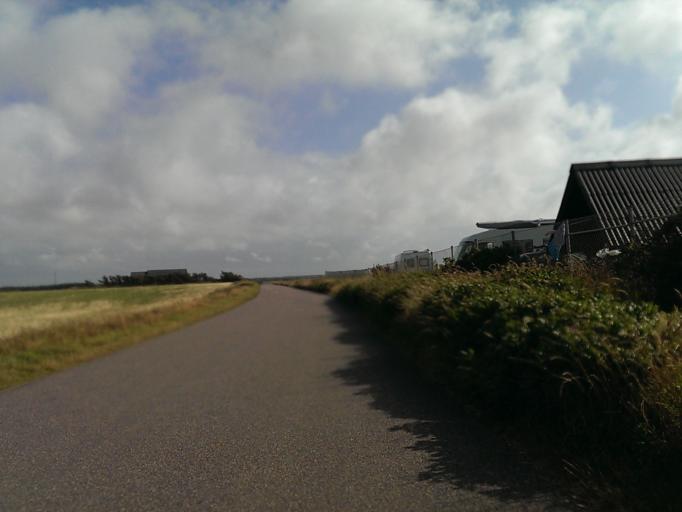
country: DK
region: North Denmark
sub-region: Jammerbugt Kommune
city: Pandrup
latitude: 57.3852
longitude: 9.7257
